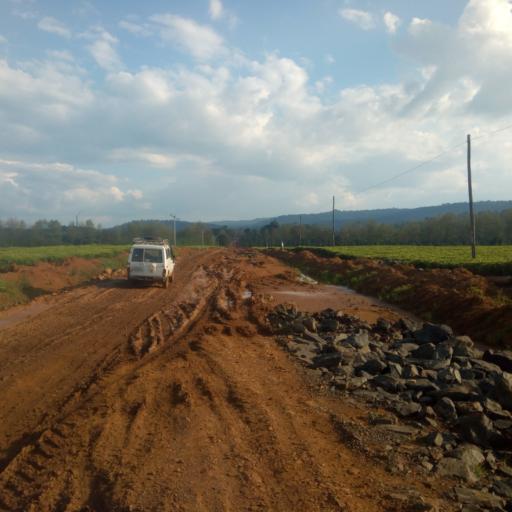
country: ET
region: Oromiya
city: Gore
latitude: 7.8546
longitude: 35.4756
